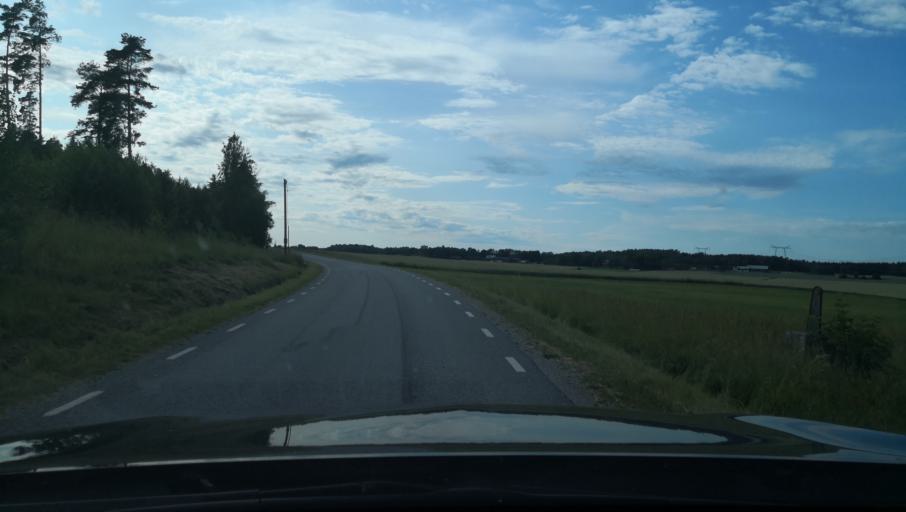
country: SE
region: Uppsala
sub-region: Enkopings Kommun
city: Orsundsbro
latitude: 59.6920
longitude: 17.3569
